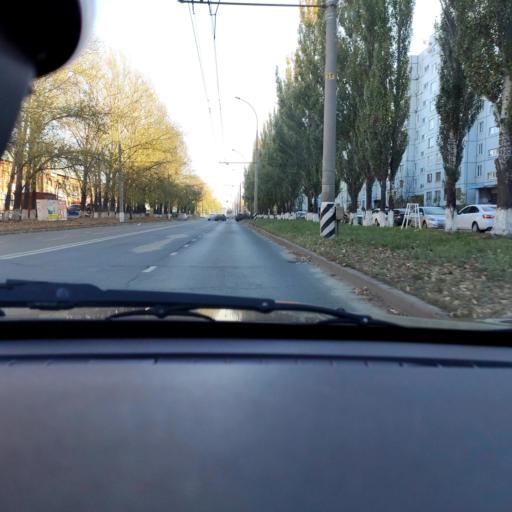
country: RU
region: Samara
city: Tol'yatti
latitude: 53.5369
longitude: 49.2915
